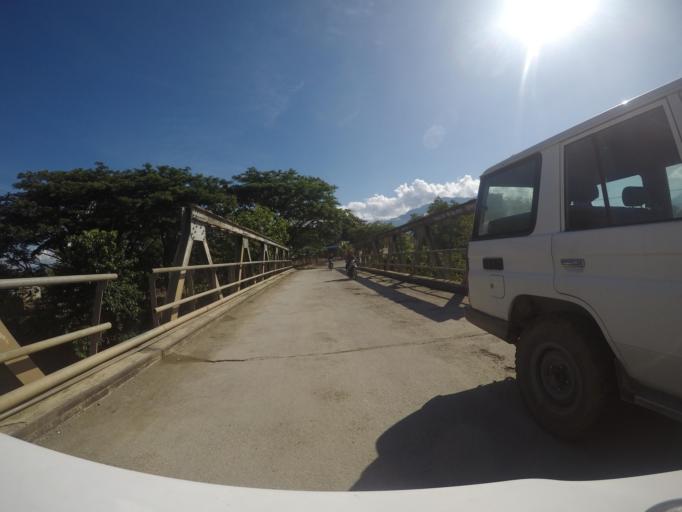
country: TL
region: Bobonaro
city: Maliana
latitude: -8.9920
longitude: 125.1942
